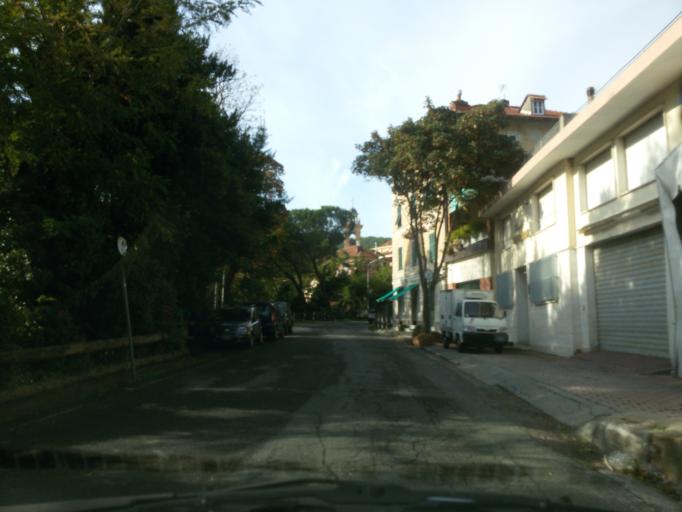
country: IT
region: Liguria
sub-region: Provincia di Genova
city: Piccarello
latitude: 44.4898
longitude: 8.9723
